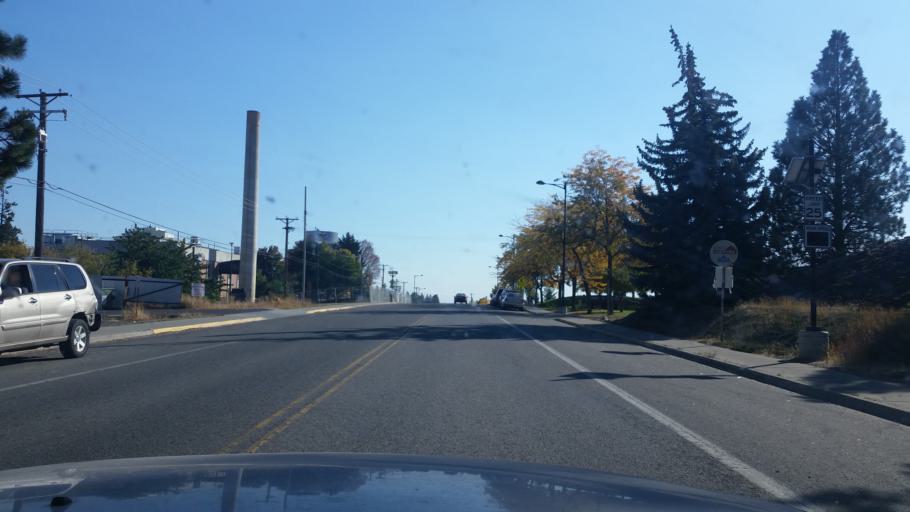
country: US
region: Washington
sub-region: Spokane County
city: Cheney
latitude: 47.4955
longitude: -117.5866
